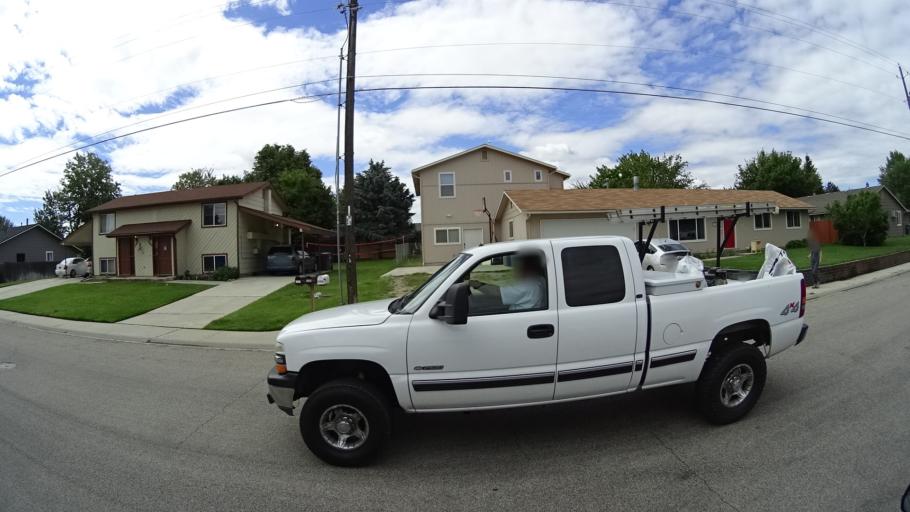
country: US
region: Idaho
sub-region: Ada County
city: Boise
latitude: 43.5716
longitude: -116.1689
